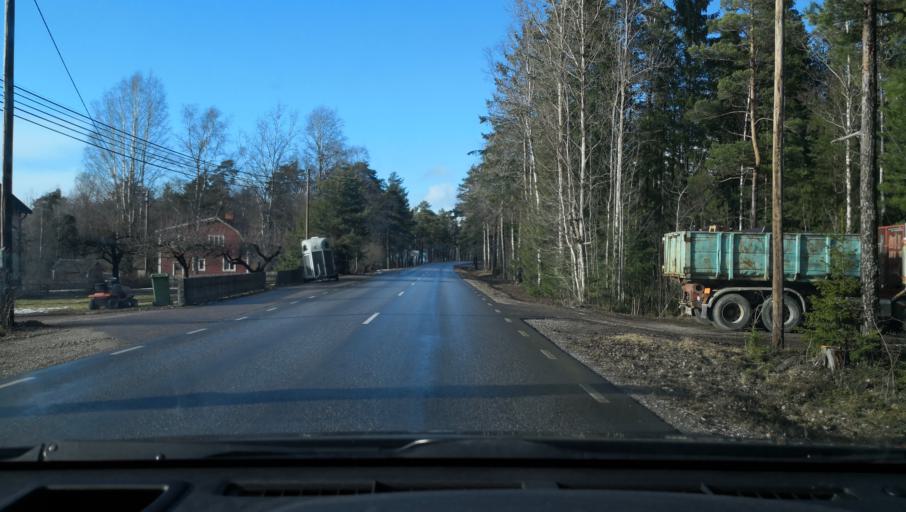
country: SE
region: Vaestmanland
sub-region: Arboga Kommun
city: Arboga
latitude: 59.3735
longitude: 15.8437
